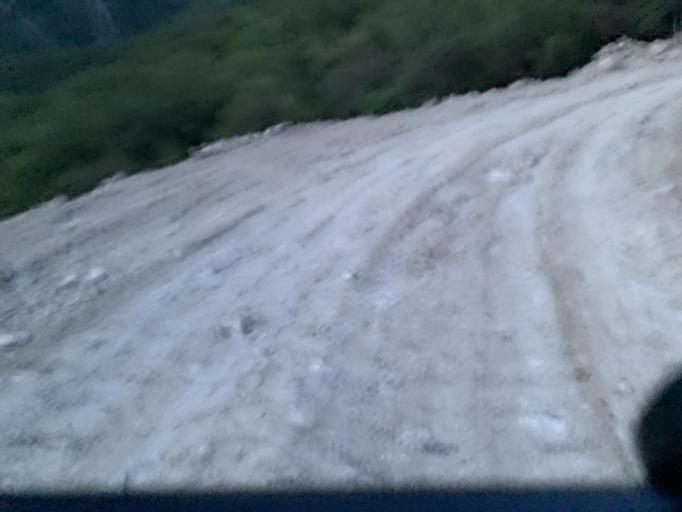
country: MX
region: Nuevo Leon
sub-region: Juarez
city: Bosques de San Pedro
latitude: 25.5159
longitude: -100.1829
